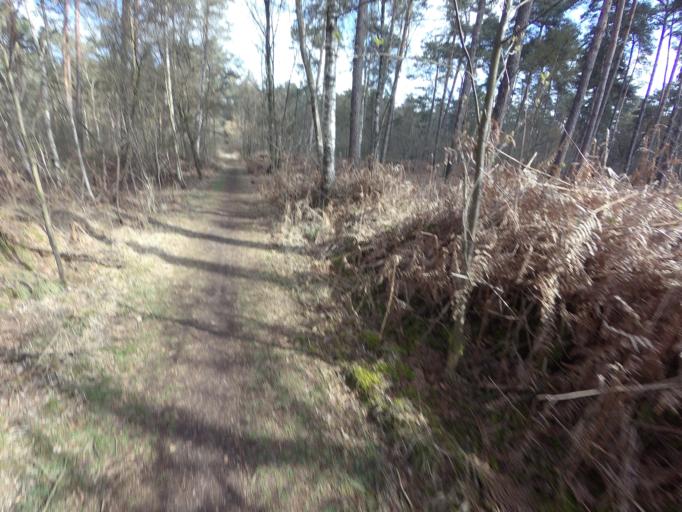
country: NL
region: Limburg
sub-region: Gemeente Roerdalen
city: Herkenbosch
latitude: 51.1713
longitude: 6.0917
